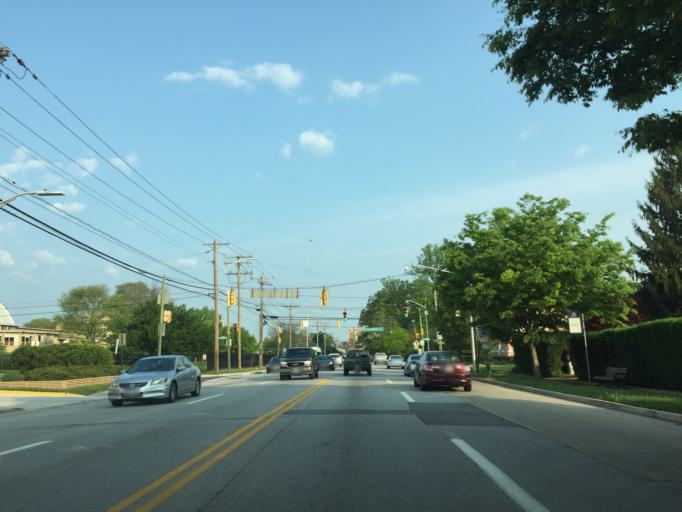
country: US
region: Maryland
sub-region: Baltimore County
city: Pikesville
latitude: 39.3585
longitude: -76.6935
